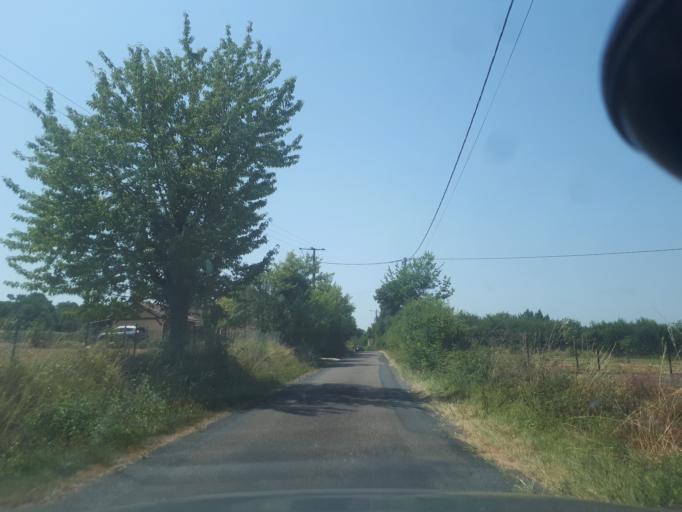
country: FR
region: Midi-Pyrenees
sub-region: Departement du Lot
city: Gourdon
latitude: 44.7540
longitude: 1.3434
